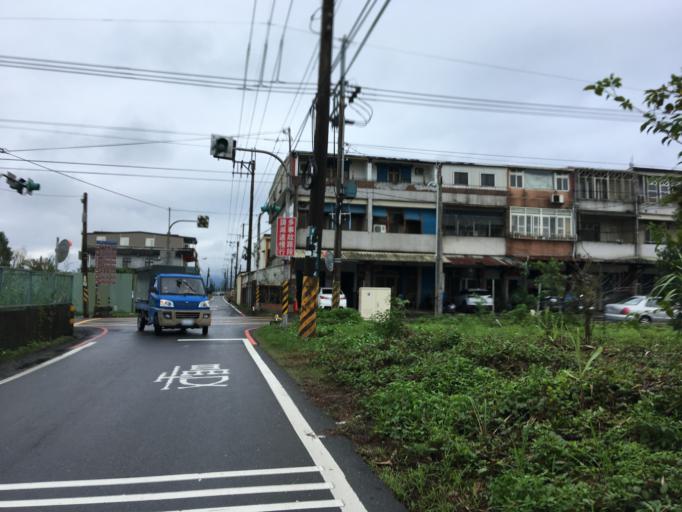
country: TW
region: Taiwan
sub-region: Yilan
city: Yilan
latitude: 24.6665
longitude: 121.7433
